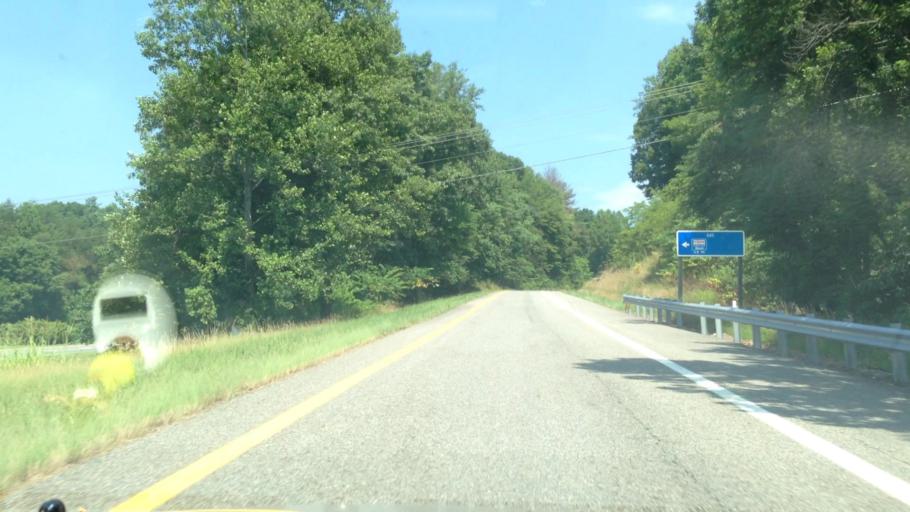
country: US
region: Virginia
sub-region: Henry County
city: Collinsville
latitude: 36.6938
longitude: -79.9503
